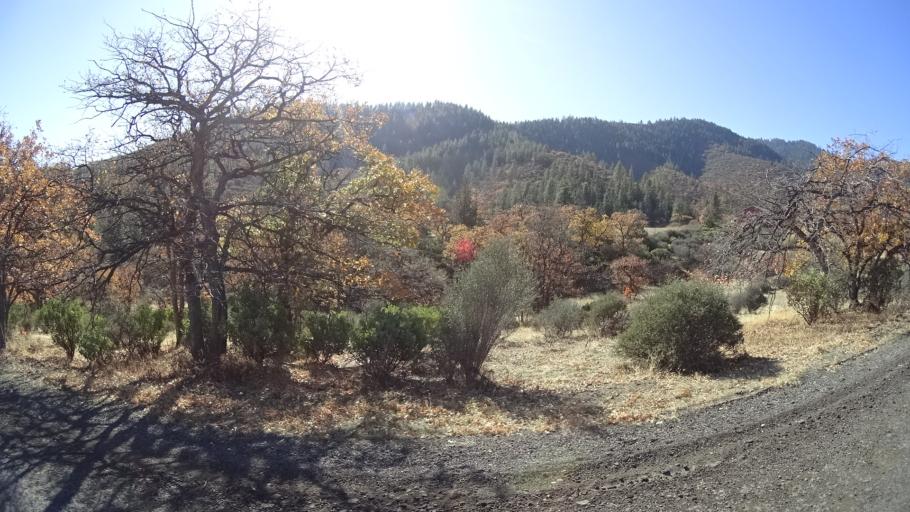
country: US
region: California
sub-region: Siskiyou County
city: Yreka
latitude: 41.7751
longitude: -122.6509
